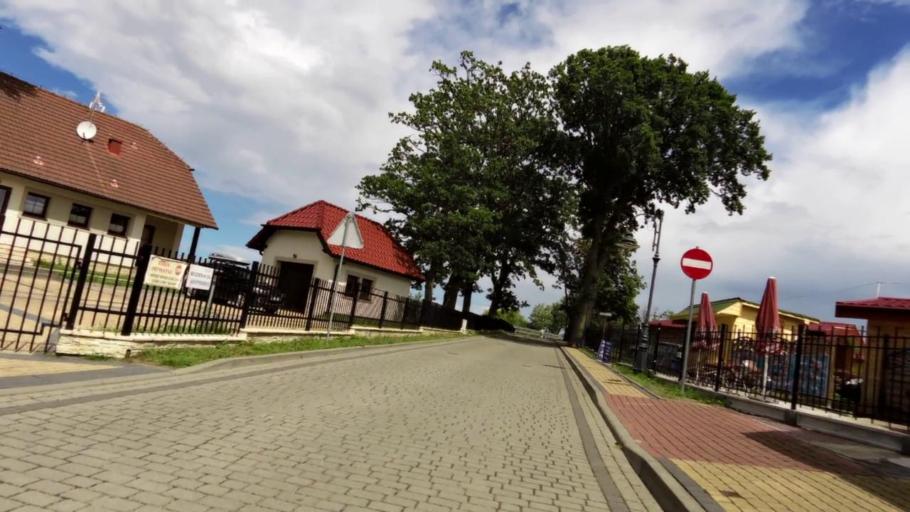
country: PL
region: West Pomeranian Voivodeship
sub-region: Powiat slawienski
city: Darlowo
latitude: 54.5385
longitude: 16.5278
